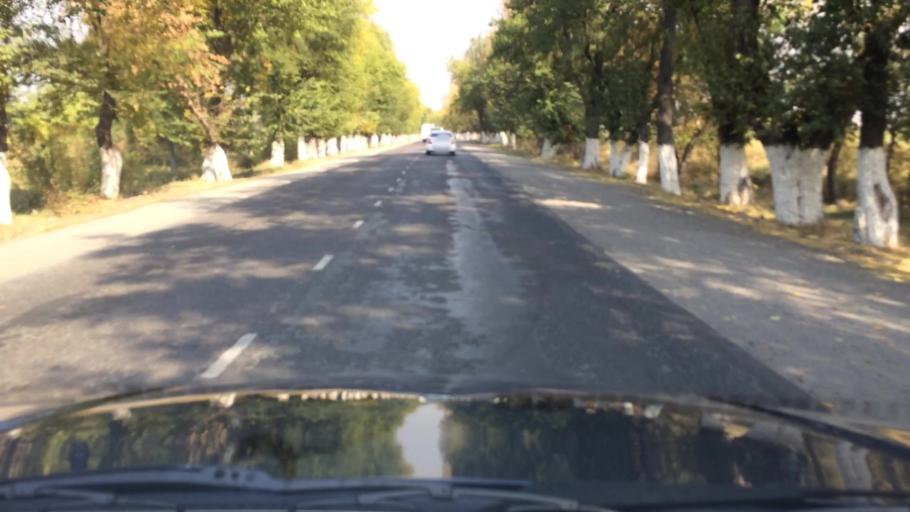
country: KG
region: Chuy
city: Lebedinovka
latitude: 42.9065
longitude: 74.6866
